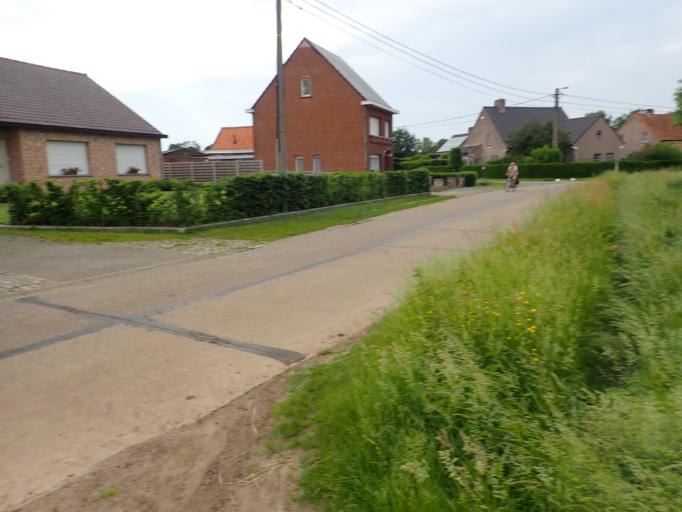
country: BE
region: Flanders
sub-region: Provincie Antwerpen
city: Vosselaar
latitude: 51.2479
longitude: 4.8843
